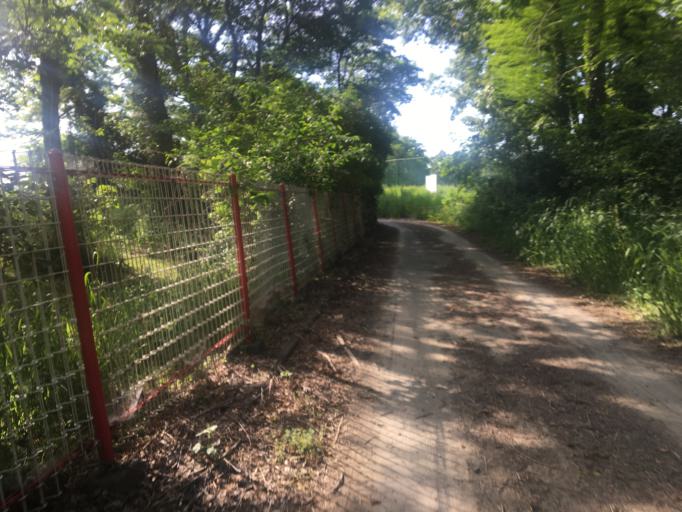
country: JP
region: Saitama
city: Shiki
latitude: 35.8551
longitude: 139.5989
